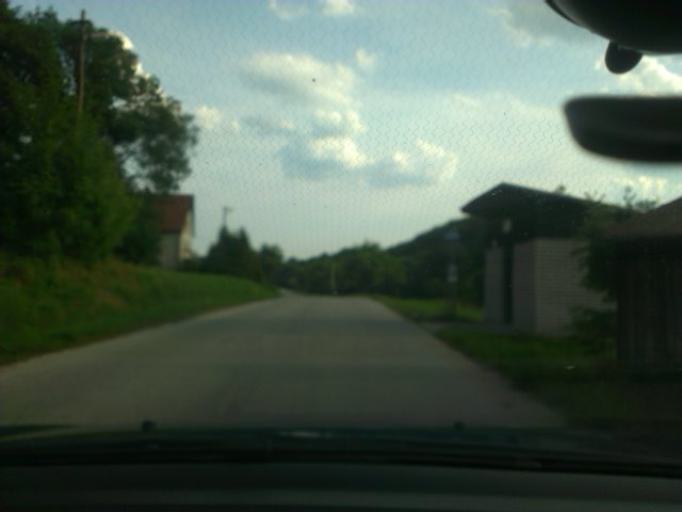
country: SK
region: Trenciansky
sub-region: Okres Myjava
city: Myjava
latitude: 48.8053
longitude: 17.5660
